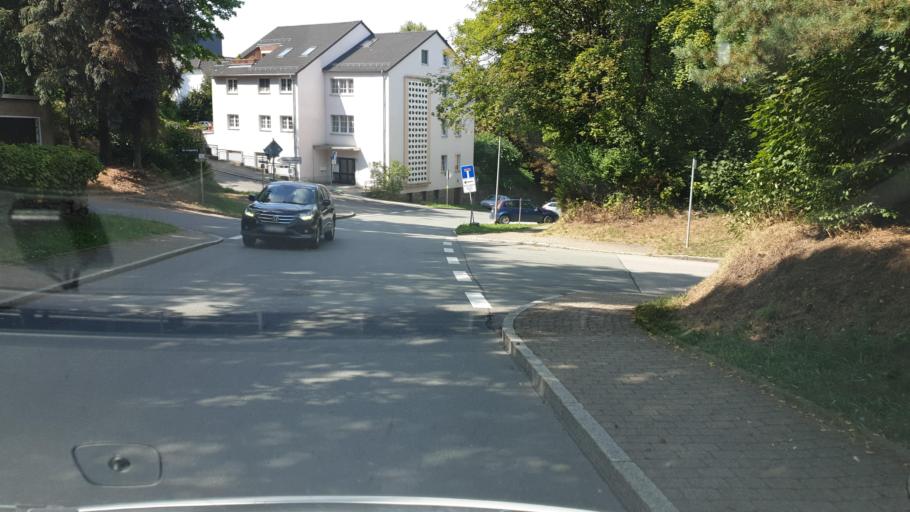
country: DE
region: Saxony
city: Zschopau
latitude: 50.7422
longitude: 13.0695
